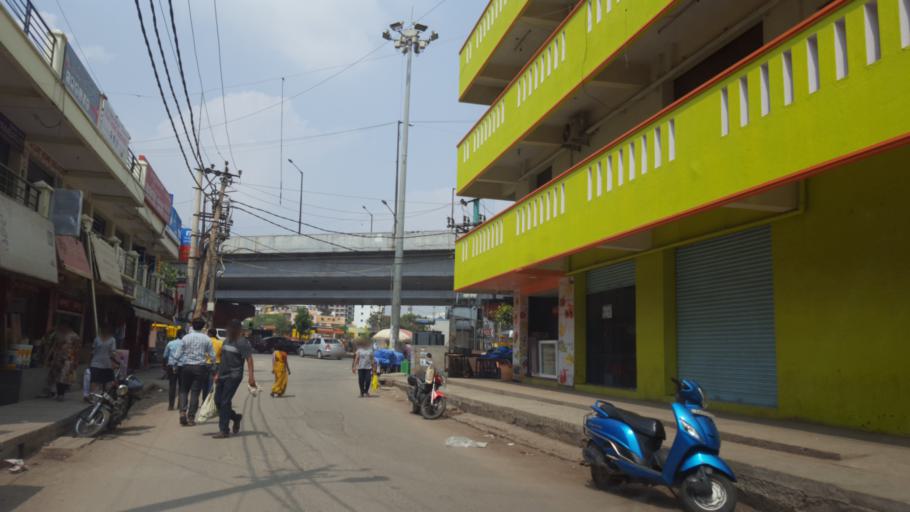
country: IN
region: Karnataka
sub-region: Bangalore Urban
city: Bangalore
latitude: 12.9906
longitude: 77.6873
